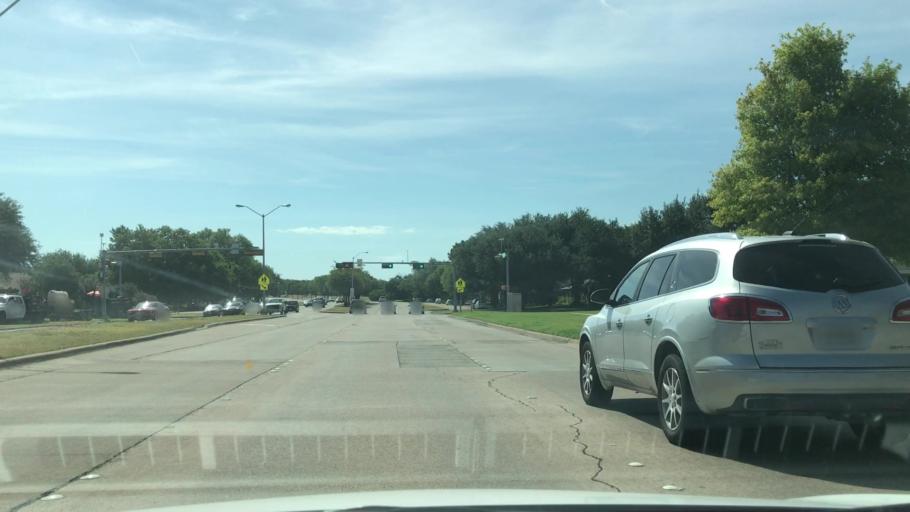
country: US
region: Texas
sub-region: Collin County
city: Plano
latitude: 33.0577
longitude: -96.7289
